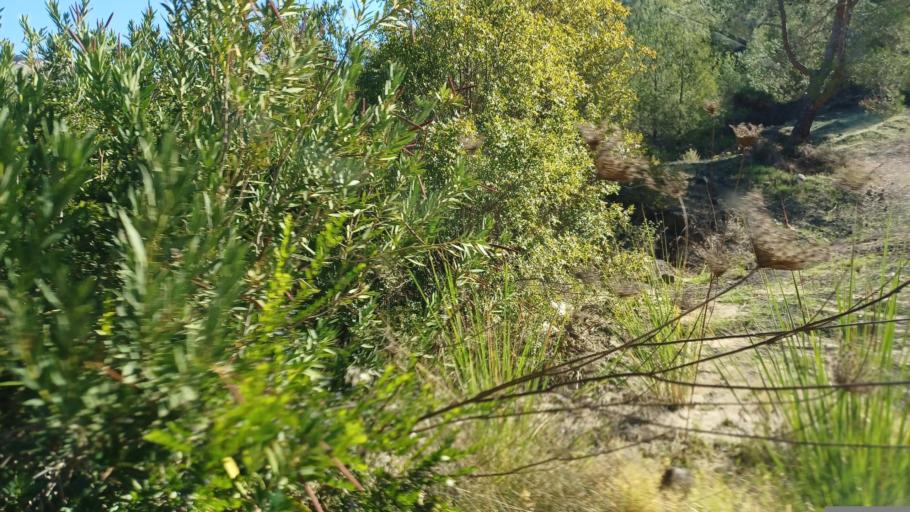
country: CY
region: Pafos
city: Polis
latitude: 35.0239
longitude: 32.4906
